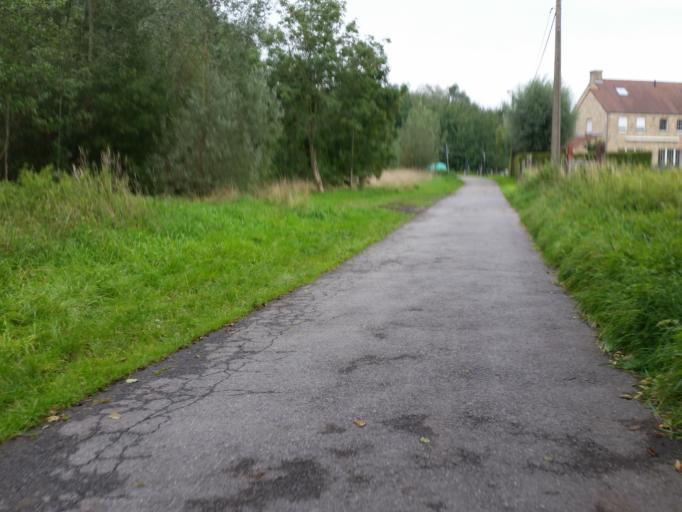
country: BE
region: Flanders
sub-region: Provincie Antwerpen
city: Kontich
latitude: 51.1242
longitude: 4.4469
